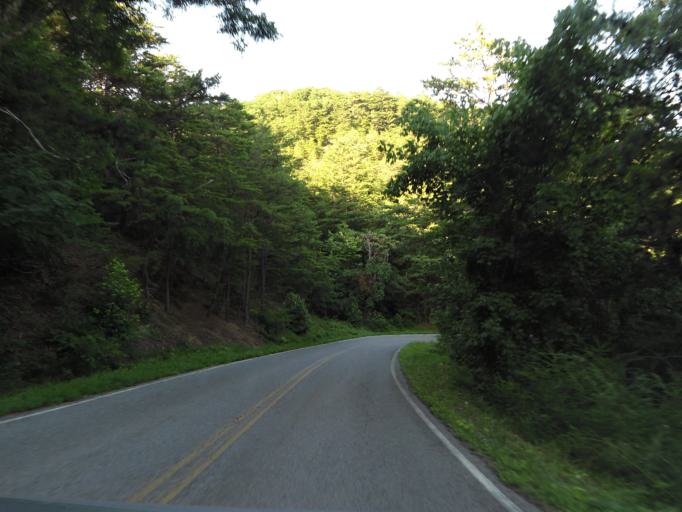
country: US
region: Tennessee
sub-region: Blount County
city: Maryville
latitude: 35.6311
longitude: -83.9463
